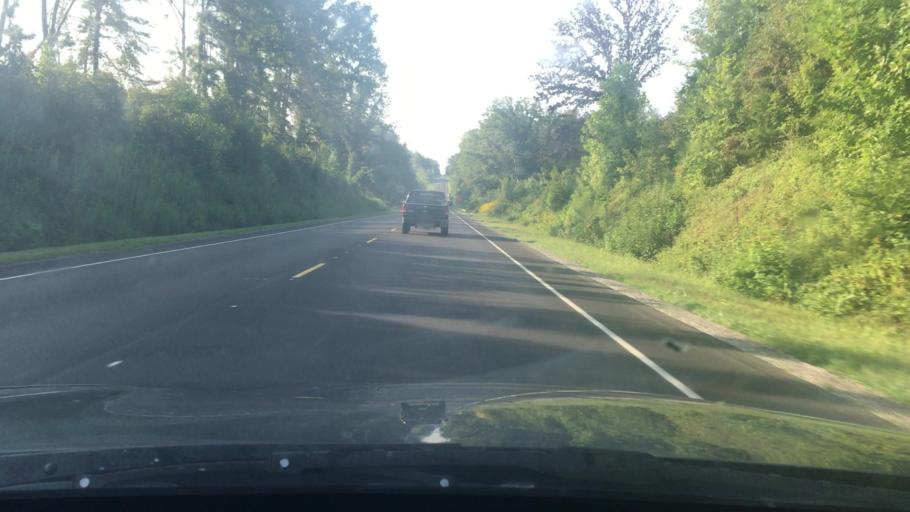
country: US
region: Virginia
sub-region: City of Danville
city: Danville
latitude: 36.5082
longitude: -79.3902
